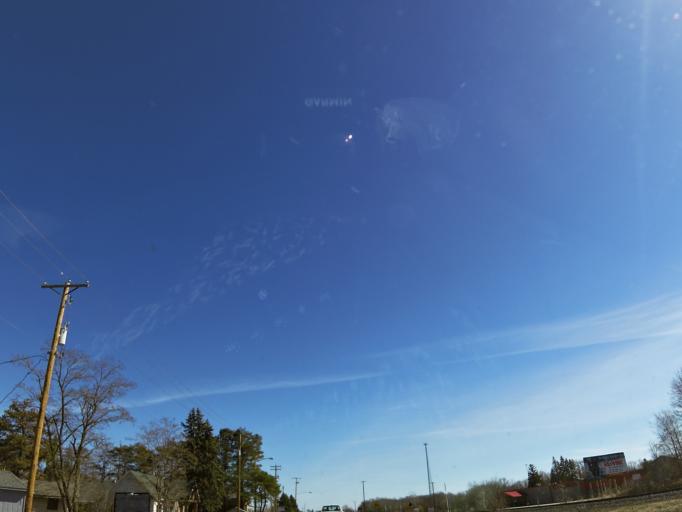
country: US
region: Minnesota
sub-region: Wright County
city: Annandale
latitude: 45.2599
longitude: -94.1207
